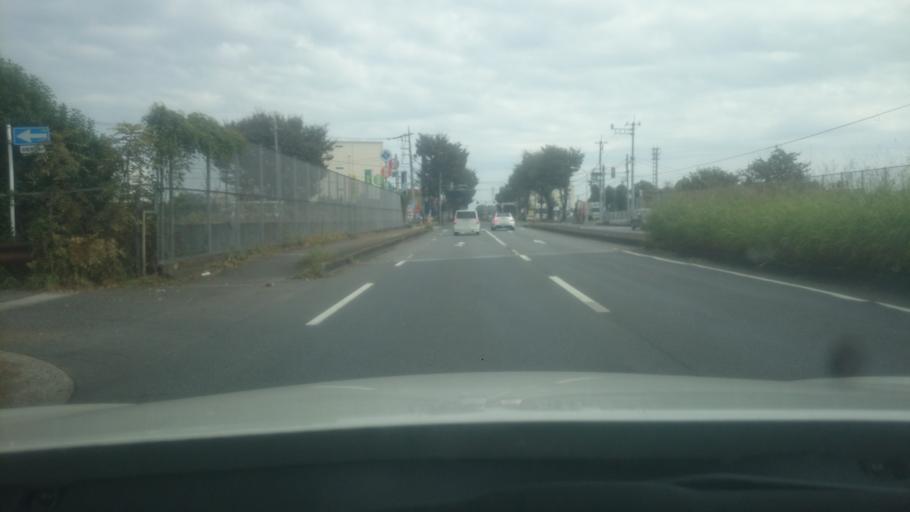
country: JP
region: Saitama
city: Oi
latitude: 35.8101
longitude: 139.5285
